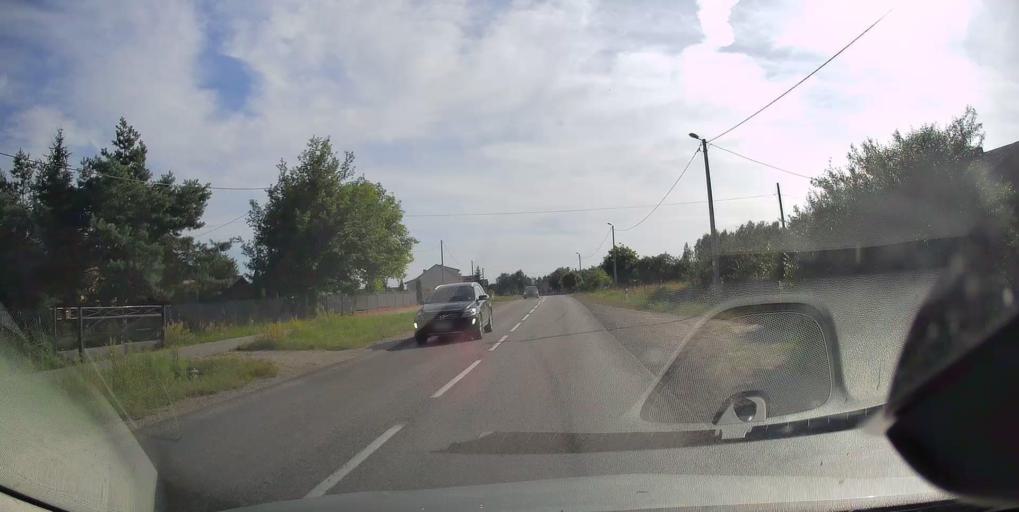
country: PL
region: Swietokrzyskie
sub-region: Powiat konecki
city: Radoszyce
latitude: 51.0886
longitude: 20.2915
